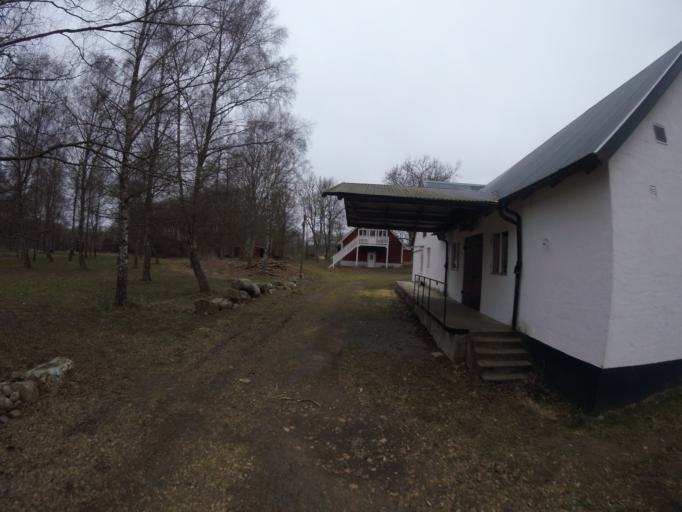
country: SE
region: Skane
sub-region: Simrishamns Kommun
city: Kivik
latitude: 55.5937
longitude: 14.1802
